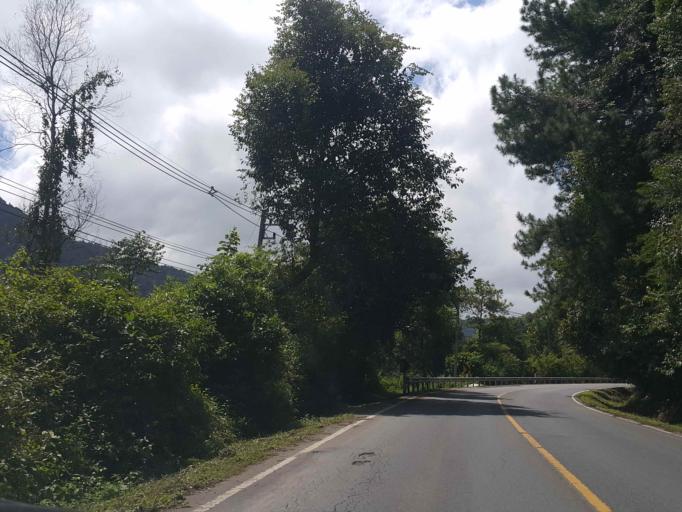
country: TH
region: Chiang Mai
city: Chom Thong
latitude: 18.5432
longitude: 98.5468
